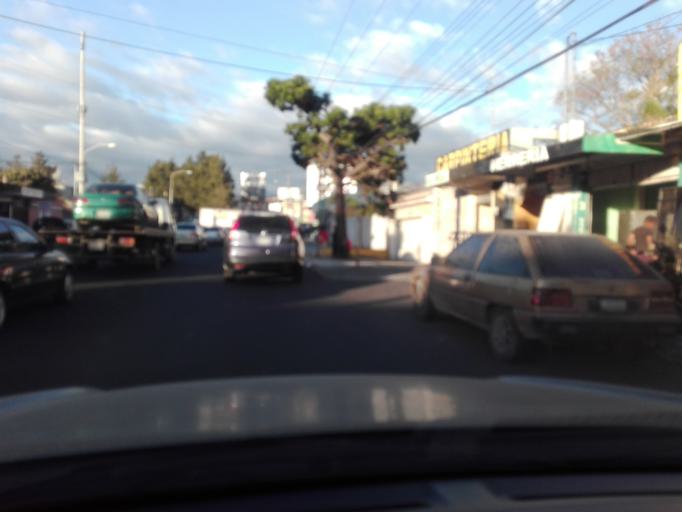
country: GT
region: Guatemala
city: Mixco
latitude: 14.5898
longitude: -90.5789
